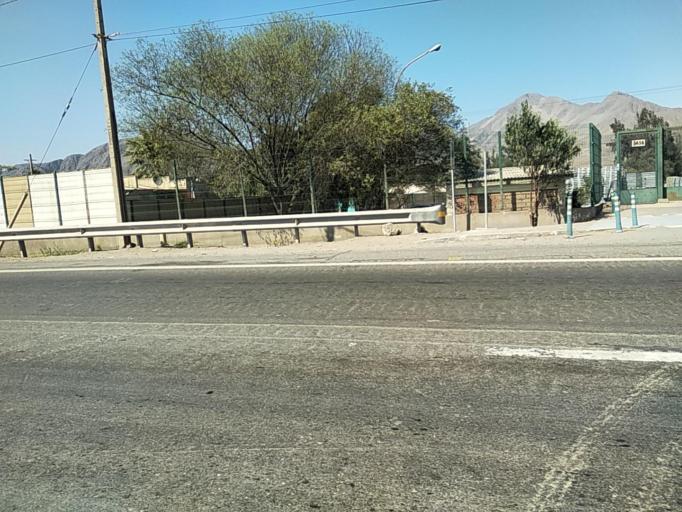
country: CL
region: Atacama
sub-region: Provincia de Copiapo
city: Copiapo
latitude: -27.4132
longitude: -70.2848
